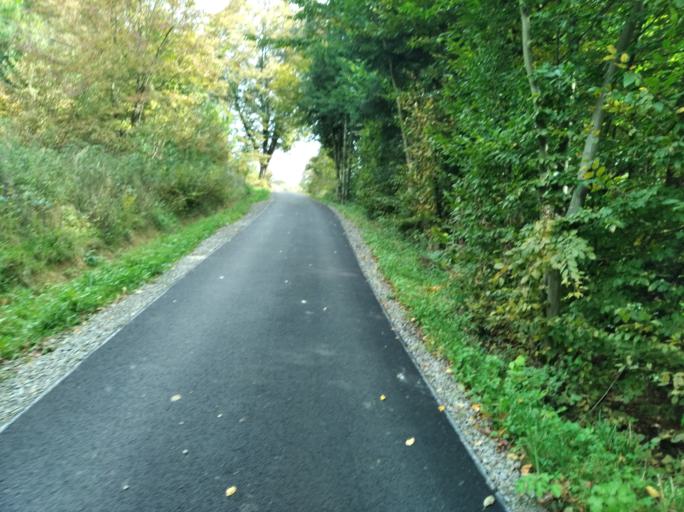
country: PL
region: Subcarpathian Voivodeship
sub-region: Powiat strzyzowski
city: Jawornik
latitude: 49.8322
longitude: 21.8978
